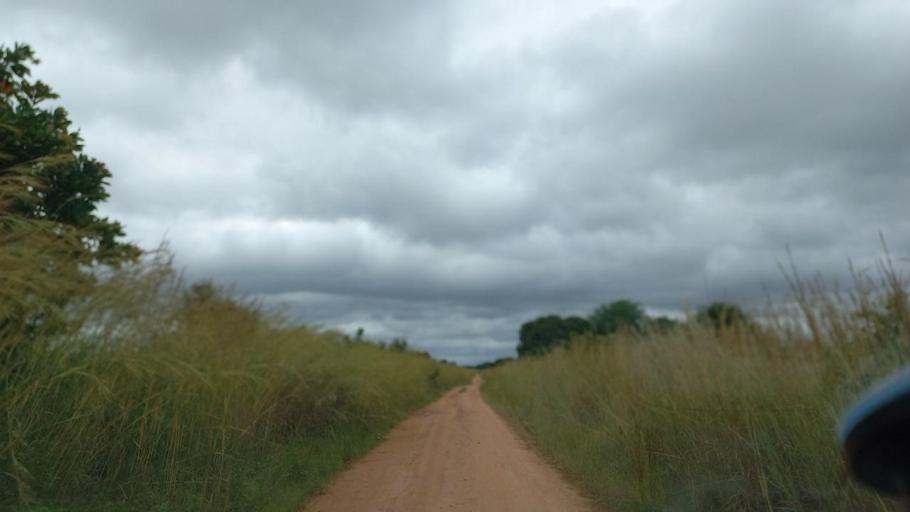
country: ZM
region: Lusaka
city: Lusaka
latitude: -15.1265
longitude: 28.3706
